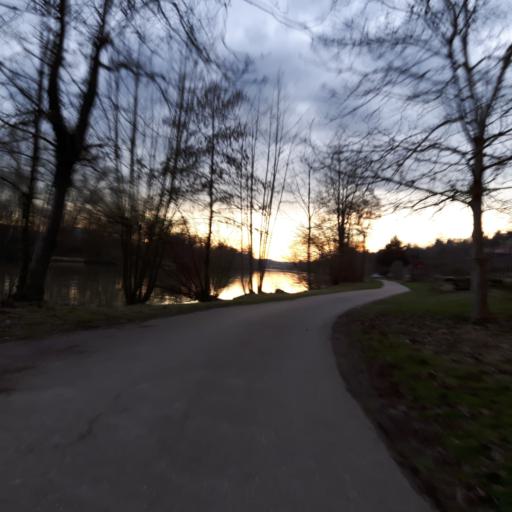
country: DE
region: Baden-Wuerttemberg
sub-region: Regierungsbezirk Stuttgart
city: Benningen am Neckar
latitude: 48.9510
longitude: 9.2276
